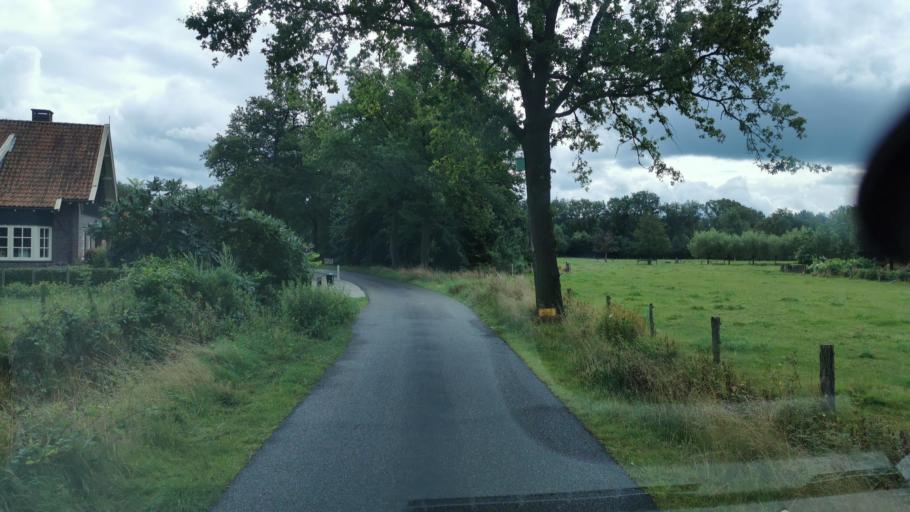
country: NL
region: Overijssel
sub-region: Gemeente Haaksbergen
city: Haaksbergen
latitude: 52.1422
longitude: 6.7147
